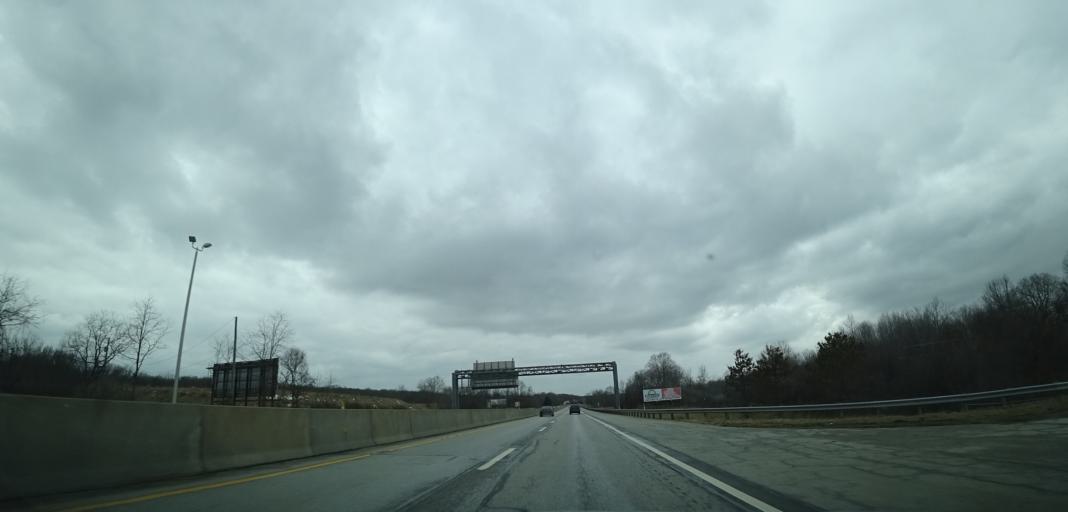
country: US
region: Pennsylvania
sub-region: Lawrence County
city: Bessemer
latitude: 40.9059
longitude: -80.5024
